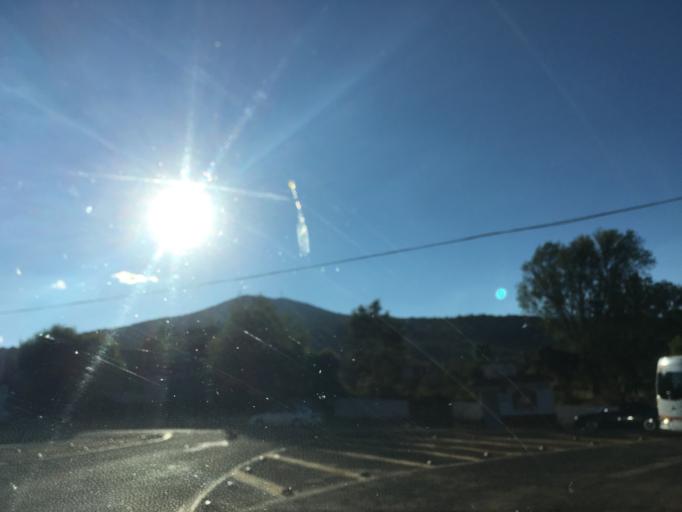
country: MX
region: Michoacan
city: Tzintzuntzan
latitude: 19.6235
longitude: -101.5767
